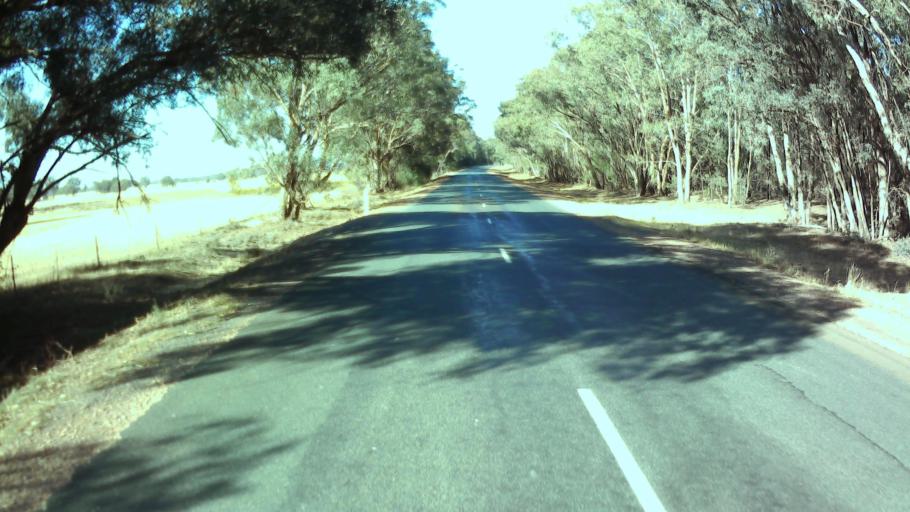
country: AU
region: New South Wales
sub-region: Weddin
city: Grenfell
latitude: -34.0110
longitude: 148.1179
